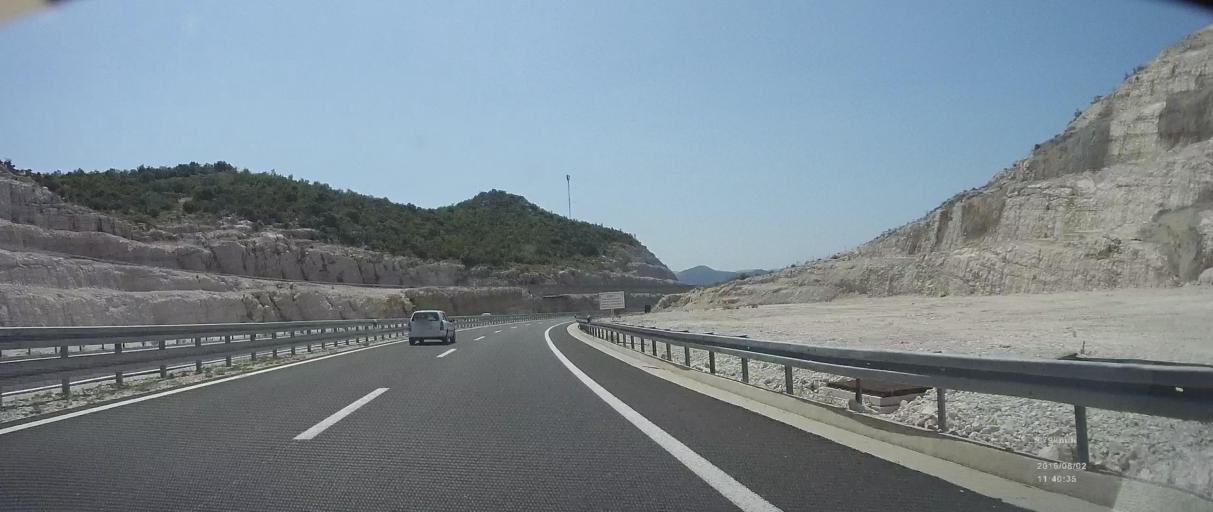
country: HR
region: Dubrovacko-Neretvanska
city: Komin
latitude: 43.0731
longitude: 17.4927
